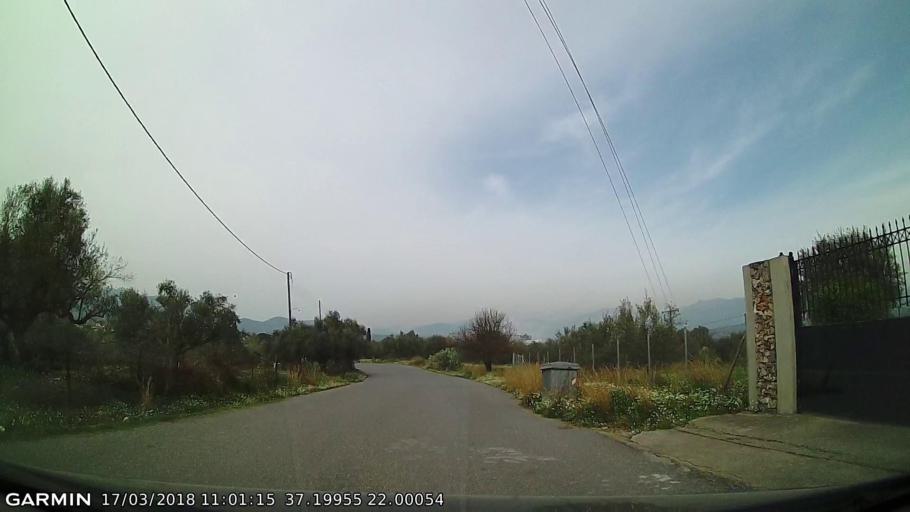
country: GR
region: Peloponnese
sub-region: Nomos Messinias
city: Meligalas
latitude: 37.1996
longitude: 22.0004
